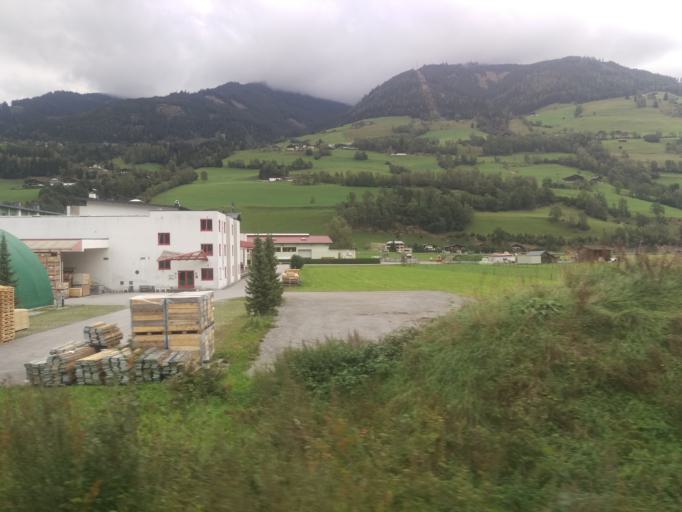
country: AT
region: Salzburg
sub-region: Politischer Bezirk Zell am See
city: Uttendorf
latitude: 47.2806
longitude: 12.5889
